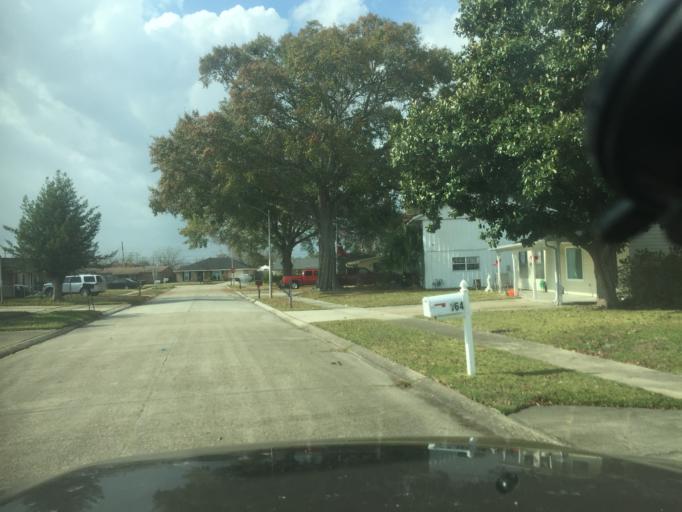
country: US
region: Louisiana
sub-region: Jefferson Parish
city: Avondale
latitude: 29.9120
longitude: -90.2053
